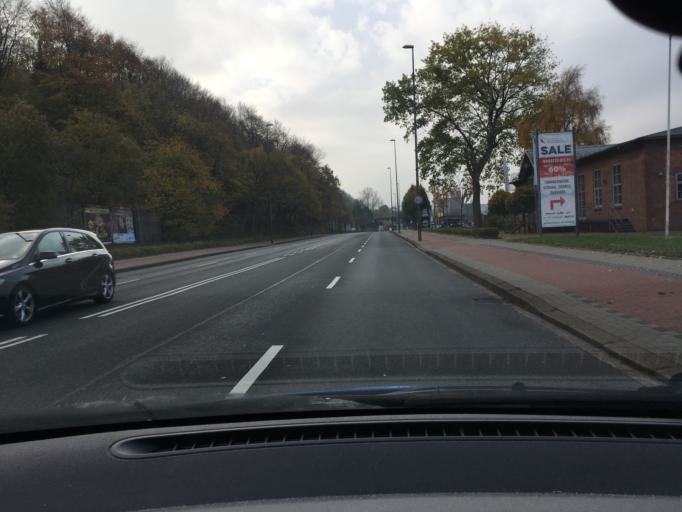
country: DE
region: Schleswig-Holstein
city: Flensburg
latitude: 54.8027
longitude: 9.4438
